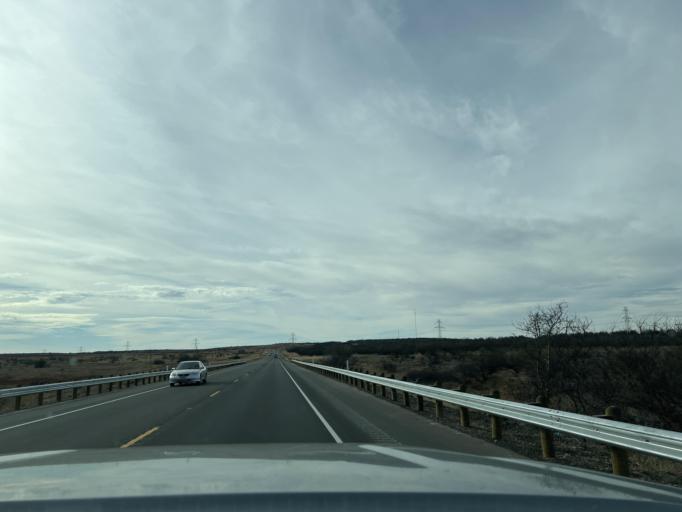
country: US
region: Texas
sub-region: Shackelford County
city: Albany
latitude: 32.7057
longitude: -99.3938
